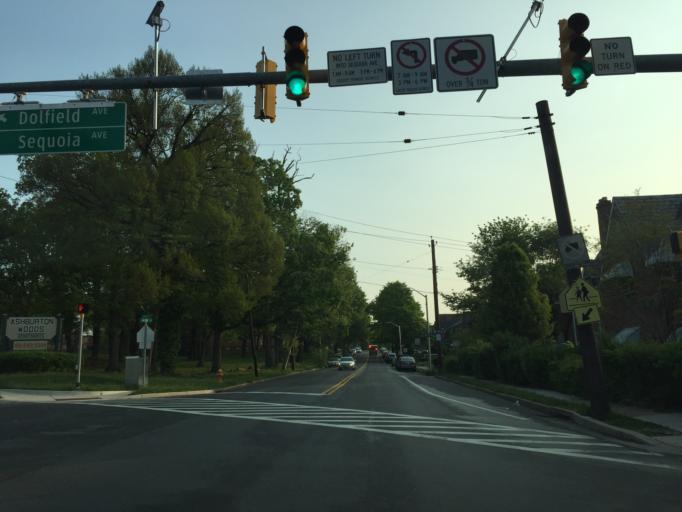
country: US
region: Maryland
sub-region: Baltimore County
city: Lochearn
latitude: 39.3288
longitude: -76.6692
